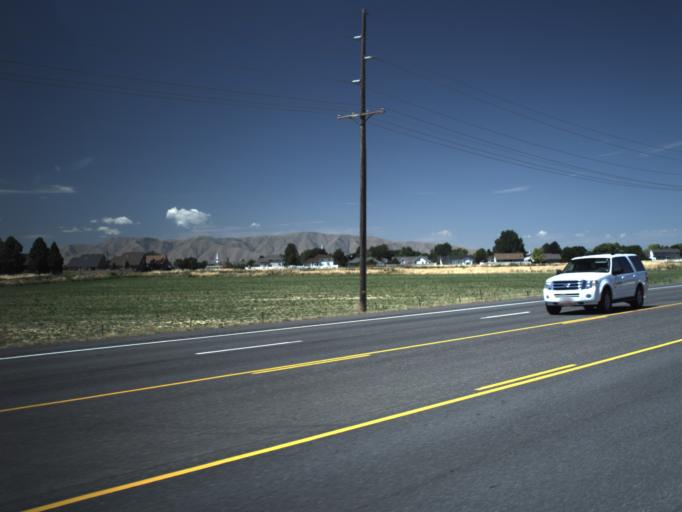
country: US
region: Utah
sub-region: Utah County
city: Spanish Fork
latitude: 40.1014
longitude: -111.6162
